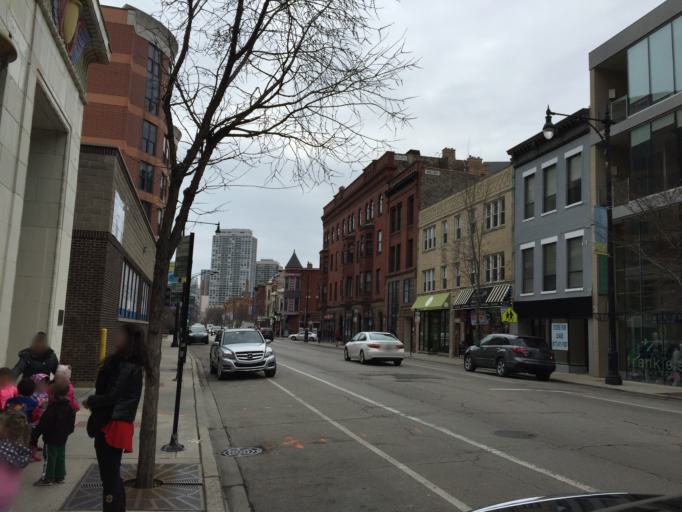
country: US
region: Illinois
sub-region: Cook County
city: Chicago
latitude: 41.9247
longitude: -87.6399
